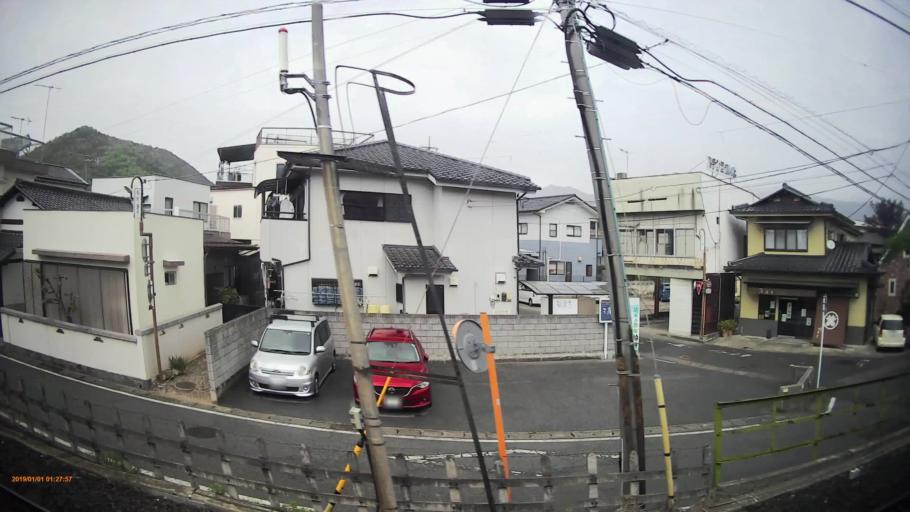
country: JP
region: Yamanashi
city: Enzan
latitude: 35.7058
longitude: 138.7311
